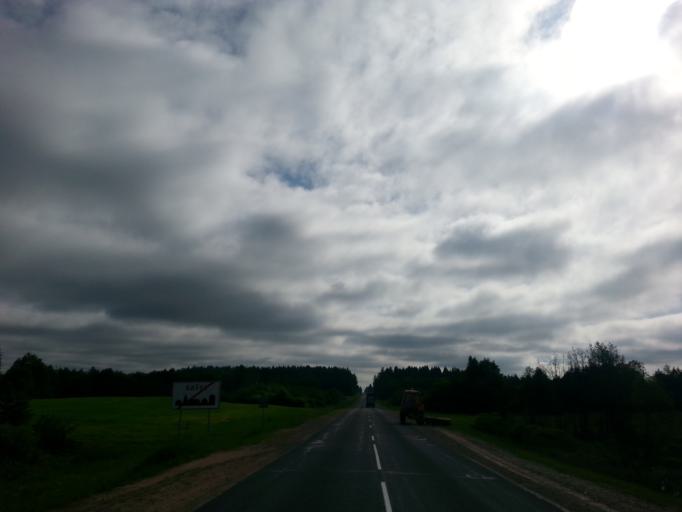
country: BY
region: Vitebsk
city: Mosar
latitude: 55.0770
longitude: 27.4308
